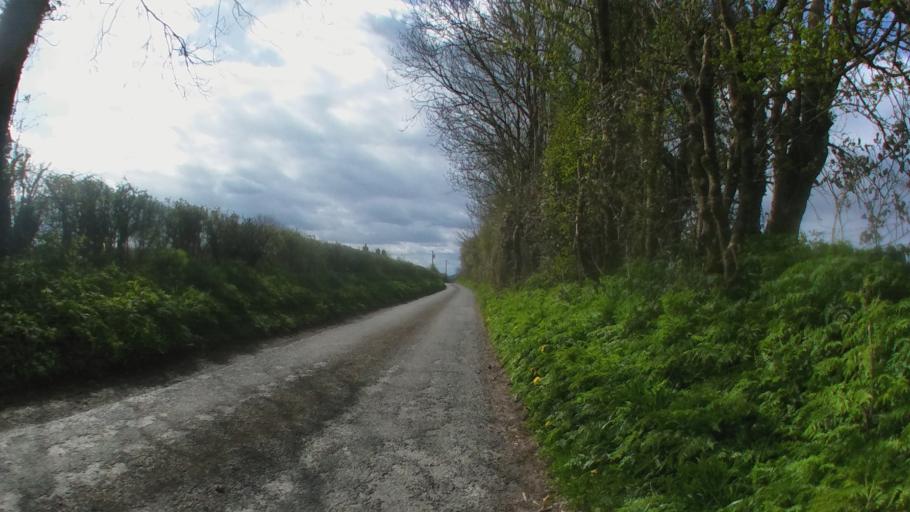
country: IE
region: Leinster
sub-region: Kilkenny
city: Kilkenny
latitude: 52.7218
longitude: -7.2285
